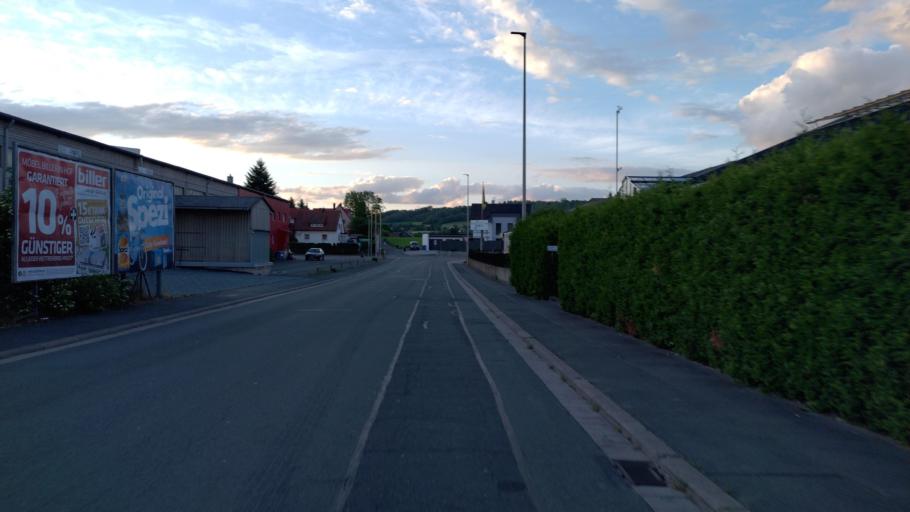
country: DE
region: Bavaria
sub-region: Upper Franconia
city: Bindlach
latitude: 49.9756
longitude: 11.6134
